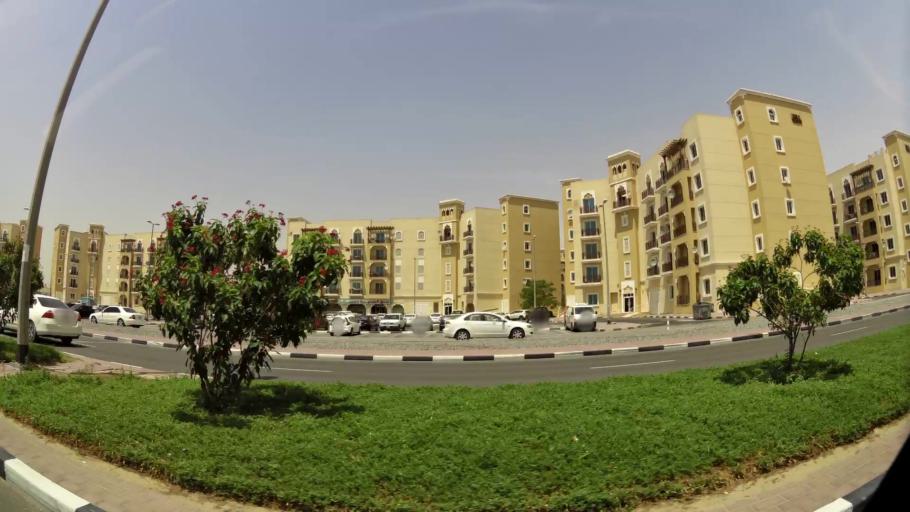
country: AE
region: Ash Shariqah
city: Sharjah
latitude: 25.1625
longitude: 55.4204
